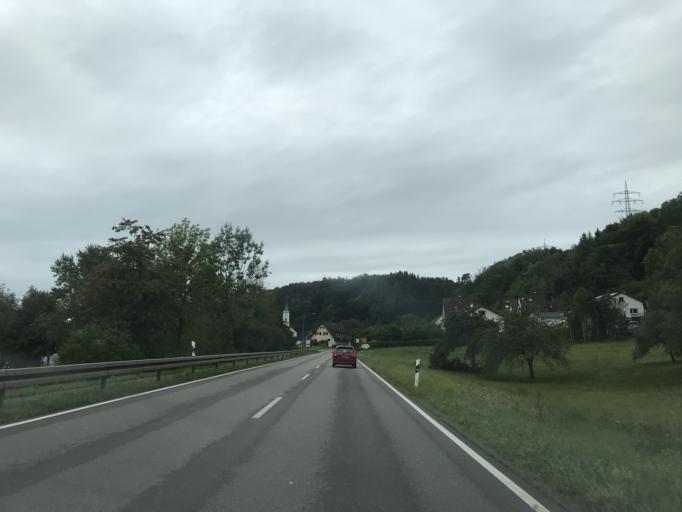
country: DE
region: Baden-Wuerttemberg
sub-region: Freiburg Region
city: Schworstadt
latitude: 47.5920
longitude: 7.8879
